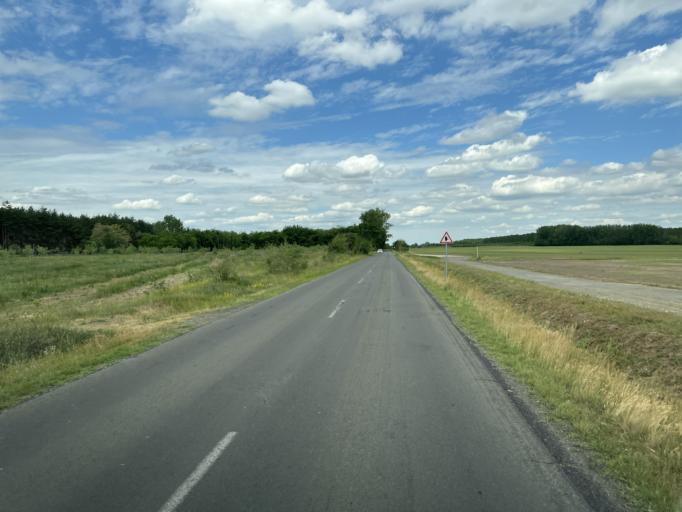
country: HU
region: Pest
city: Toalmas
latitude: 47.4848
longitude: 19.6880
